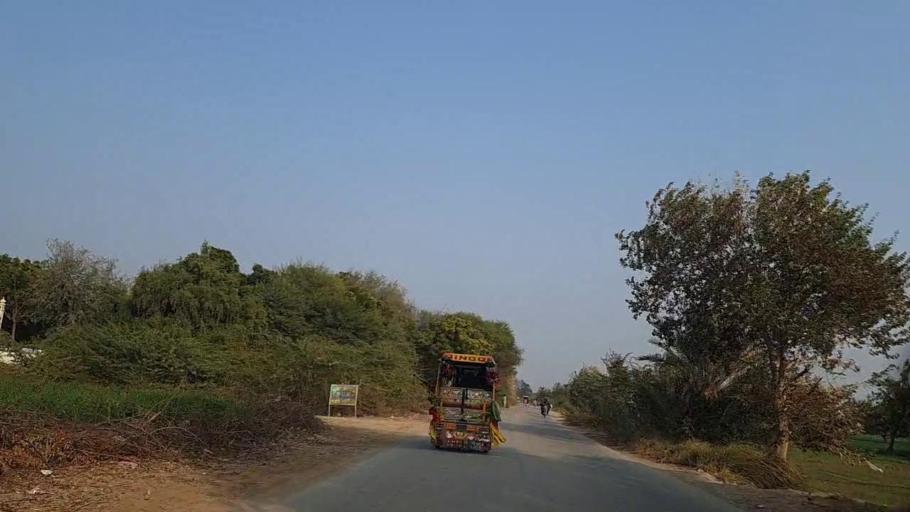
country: PK
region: Sindh
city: Sakrand
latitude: 26.1372
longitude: 68.2468
